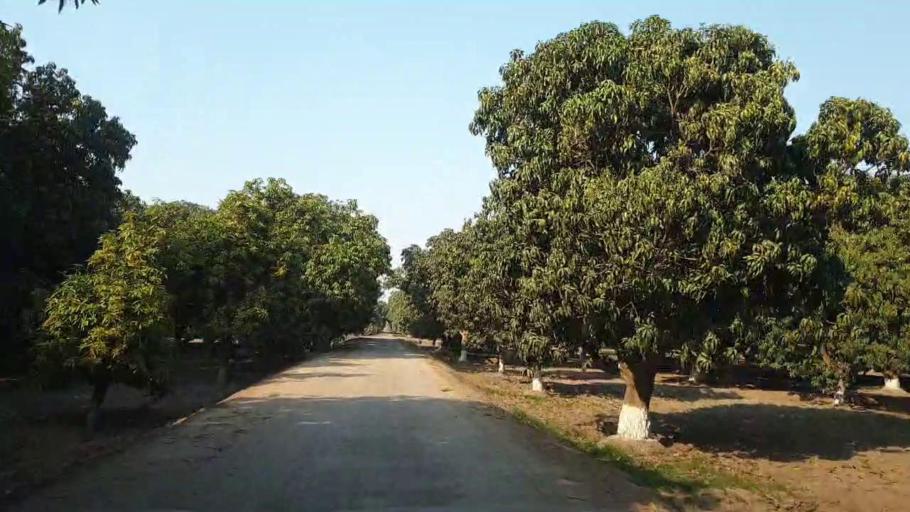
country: PK
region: Sindh
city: Tando Allahyar
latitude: 25.5767
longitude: 68.6722
